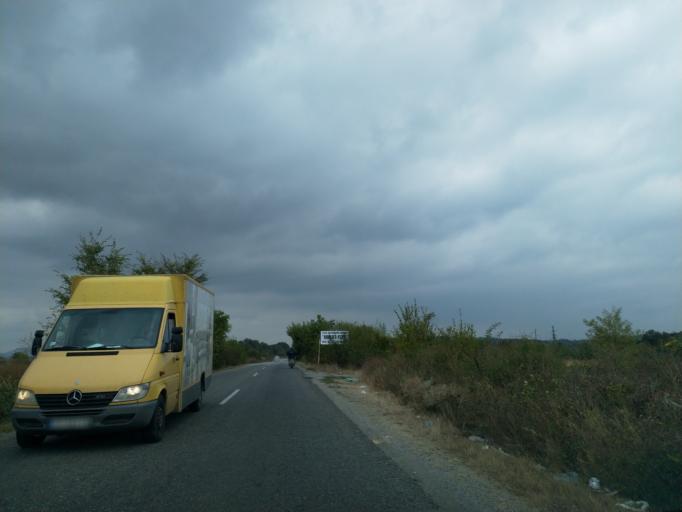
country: RS
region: Central Serbia
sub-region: Pomoravski Okrug
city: Jagodina
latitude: 44.0000
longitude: 21.2148
